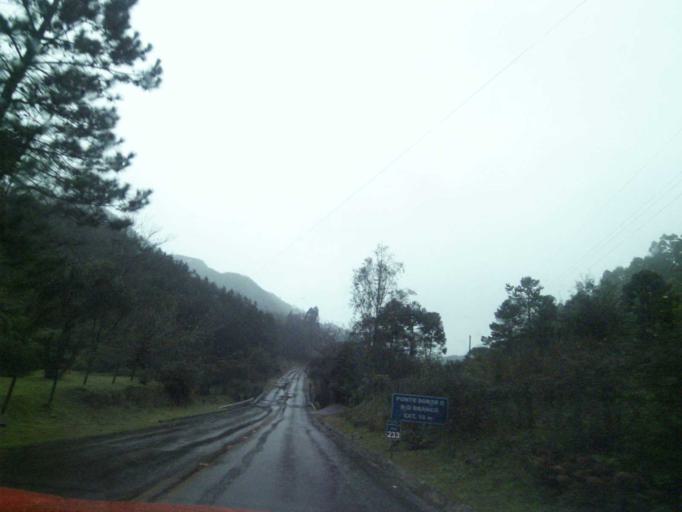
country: BR
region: Santa Catarina
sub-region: Anitapolis
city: Anitapolis
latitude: -27.7921
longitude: -49.0445
